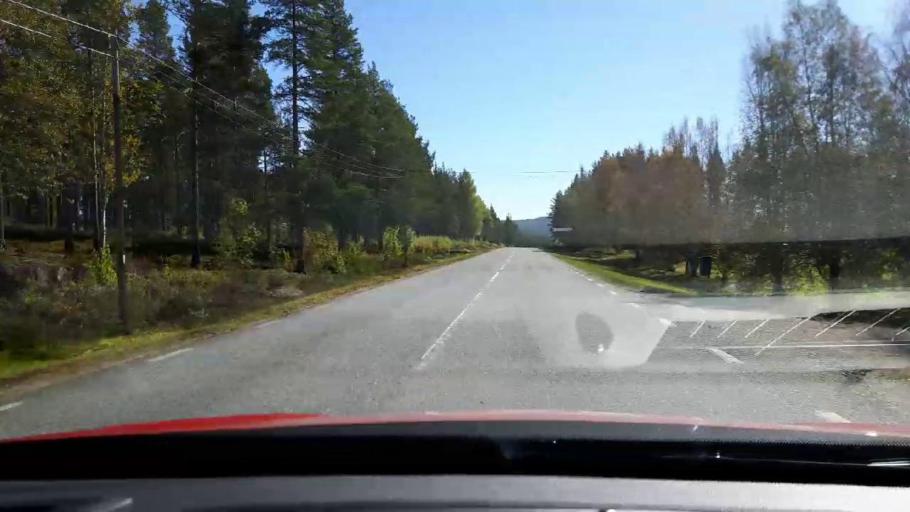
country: SE
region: Jaemtland
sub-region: Harjedalens Kommun
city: Sveg
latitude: 62.2989
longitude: 14.0691
